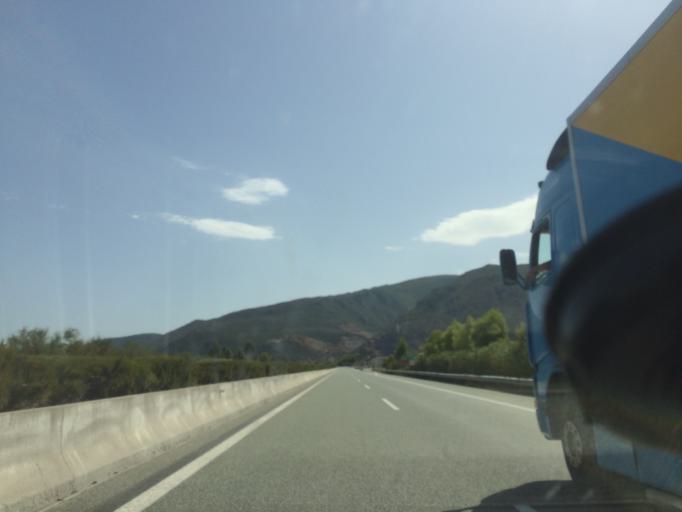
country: GR
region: Central Greece
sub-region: Nomos Fthiotidos
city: Livanates
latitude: 38.6418
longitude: 23.0823
